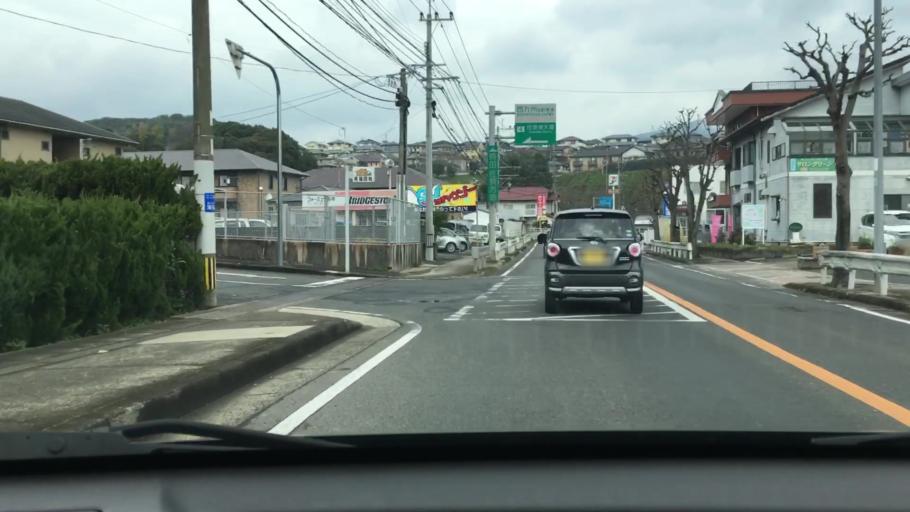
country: JP
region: Nagasaki
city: Sasebo
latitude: 33.1301
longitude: 129.7923
